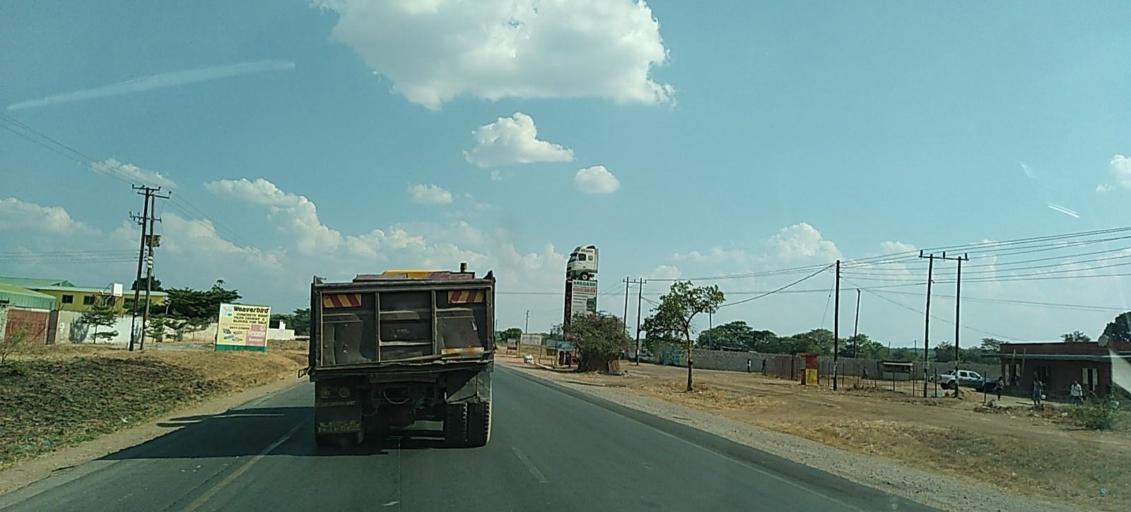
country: ZM
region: Lusaka
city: Lusaka
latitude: -15.2385
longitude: 28.2573
